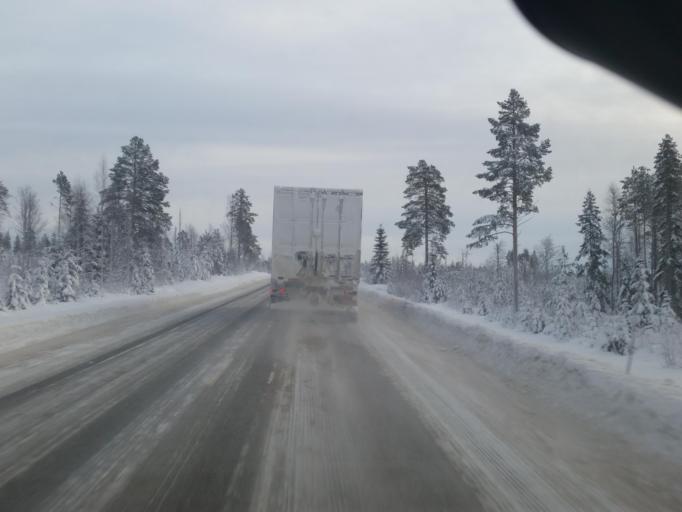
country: SE
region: Norrbotten
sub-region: Alvsbyns Kommun
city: AElvsbyn
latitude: 65.6450
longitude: 21.2673
